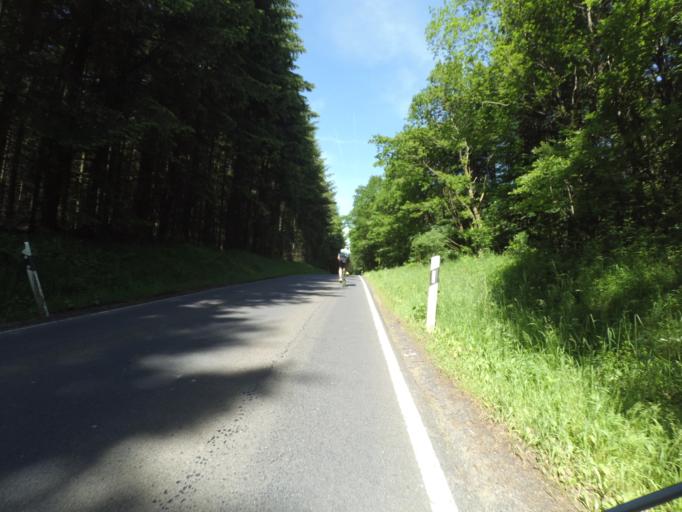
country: DE
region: Rheinland-Pfalz
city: Hauroth
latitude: 50.2426
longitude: 7.1004
